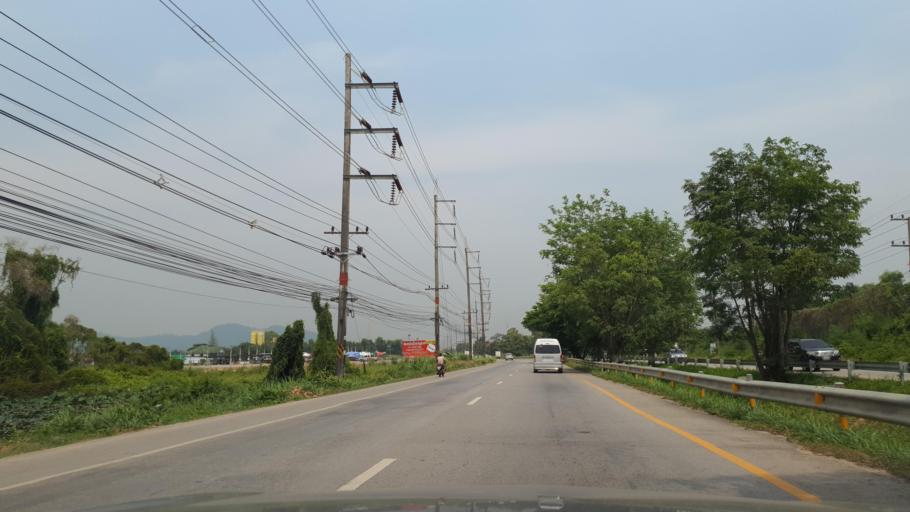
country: TH
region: Rayong
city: Rayong
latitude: 12.6391
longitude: 101.3702
